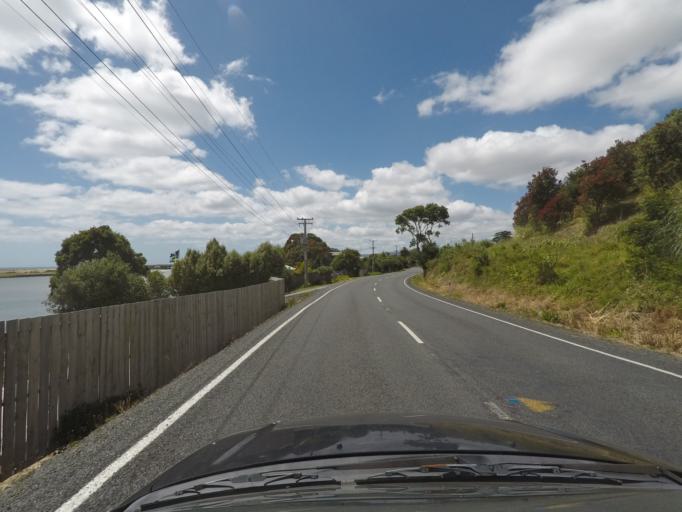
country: NZ
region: Northland
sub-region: Whangarei
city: Ruakaka
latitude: -35.9937
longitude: 174.4706
